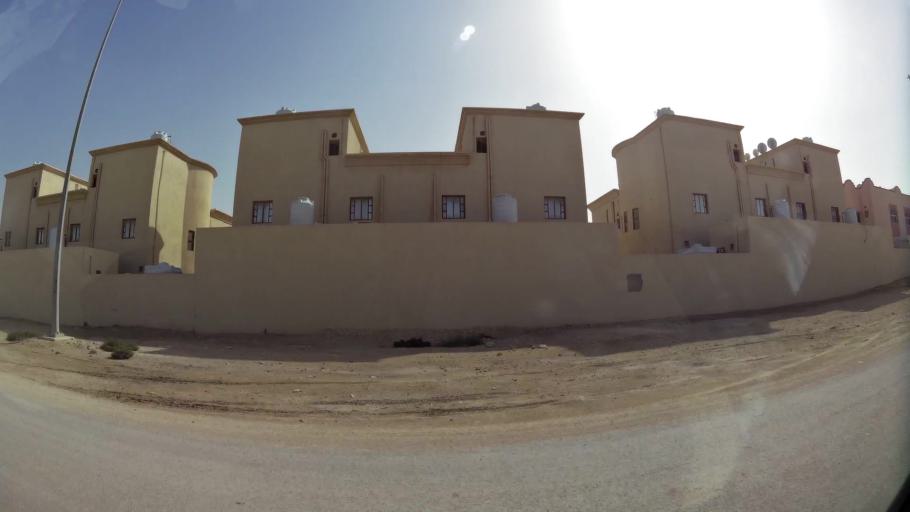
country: QA
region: Baladiyat ar Rayyan
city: Ar Rayyan
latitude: 25.3422
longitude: 51.4201
